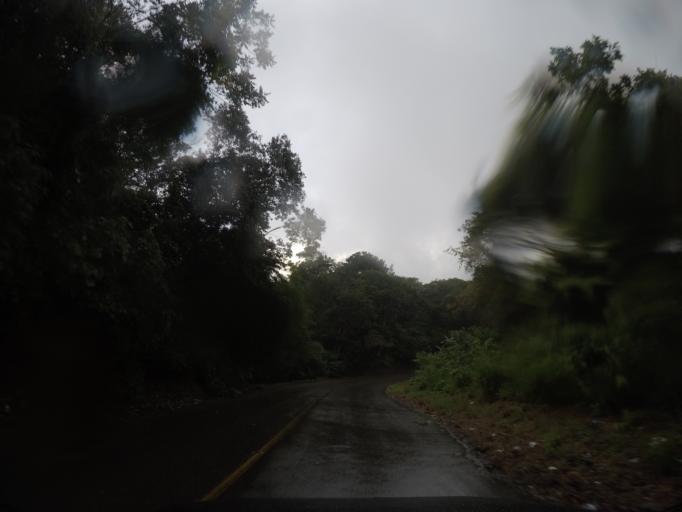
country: MX
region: Oaxaca
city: San Gabriel Mixtepec
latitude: 16.0768
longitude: -97.0859
